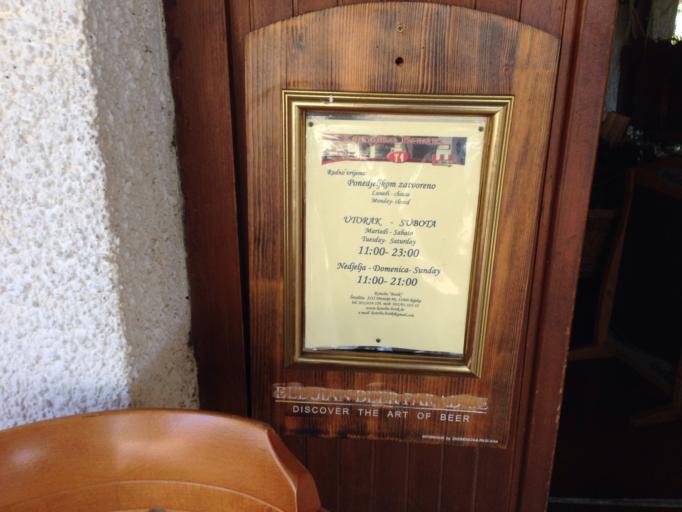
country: HR
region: Primorsko-Goranska
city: Cavle
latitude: 45.3145
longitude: 14.4702
